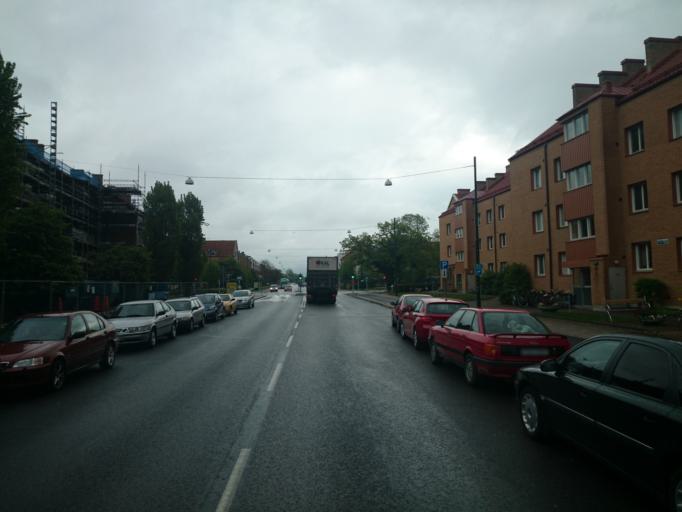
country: SE
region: Skane
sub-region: Malmo
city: Malmoe
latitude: 55.5919
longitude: 12.9702
